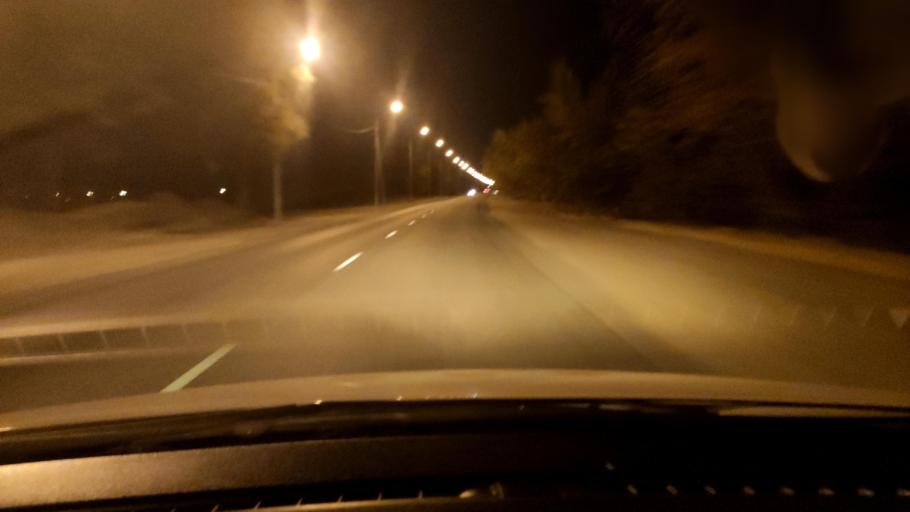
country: RU
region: Voronezj
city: Pridonskoy
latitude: 51.6906
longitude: 39.0822
